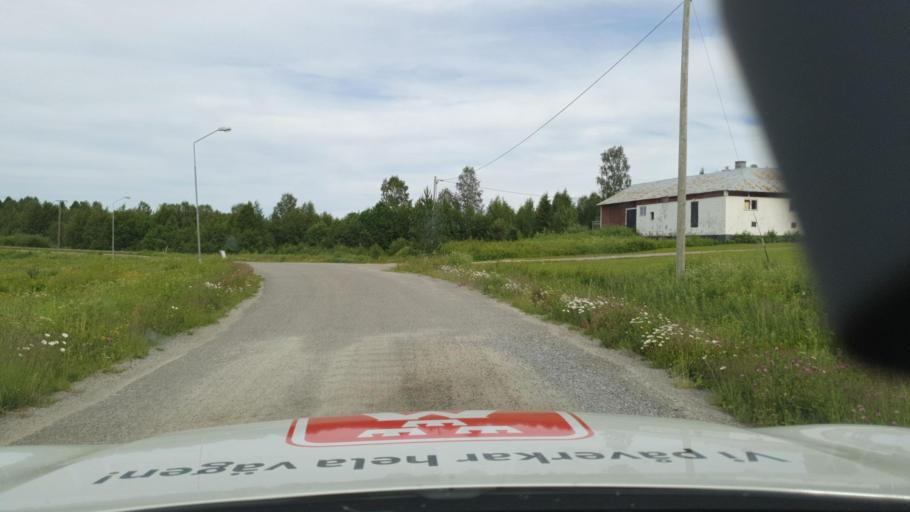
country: SE
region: Vaesterbotten
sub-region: Skelleftea Kommun
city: Viken
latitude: 64.5150
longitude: 20.9509
